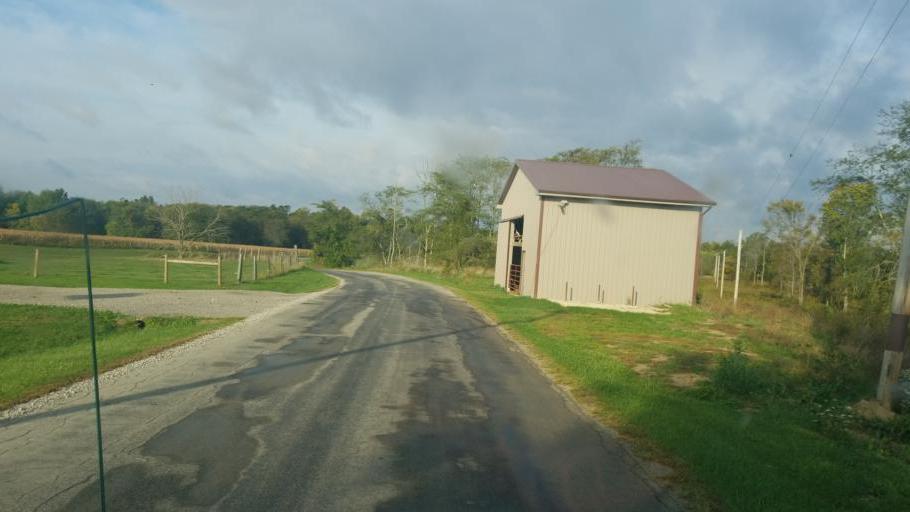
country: US
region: Ohio
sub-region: Wyandot County
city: Carey
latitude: 40.8603
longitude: -83.3703
